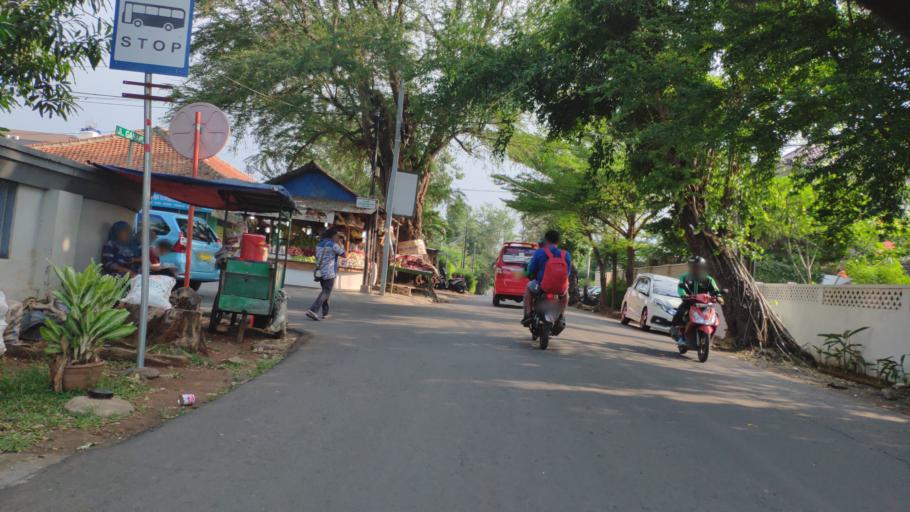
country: ID
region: Jakarta Raya
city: Jakarta
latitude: -6.2799
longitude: 106.7996
